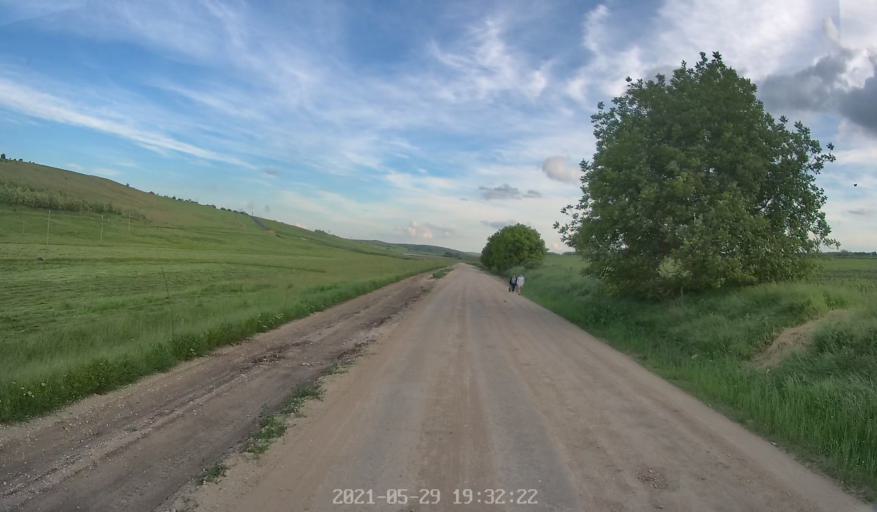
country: MD
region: Chisinau
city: Singera
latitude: 46.8323
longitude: 28.9561
